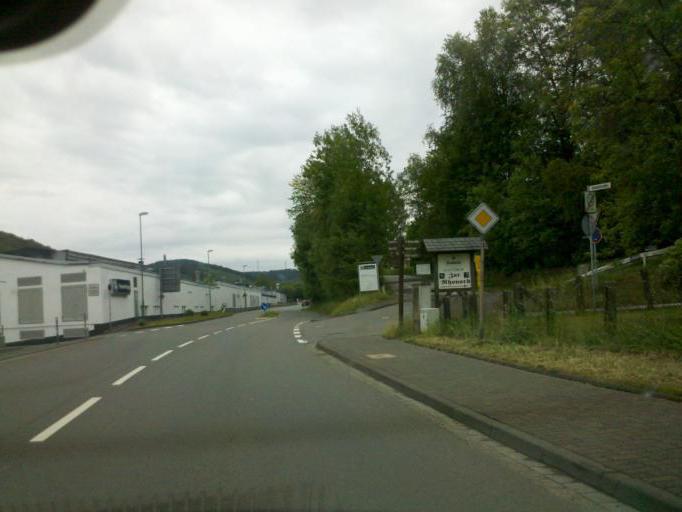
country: DE
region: North Rhine-Westphalia
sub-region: Regierungsbezirk Arnsberg
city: Olpe
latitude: 51.0371
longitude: 7.8723
